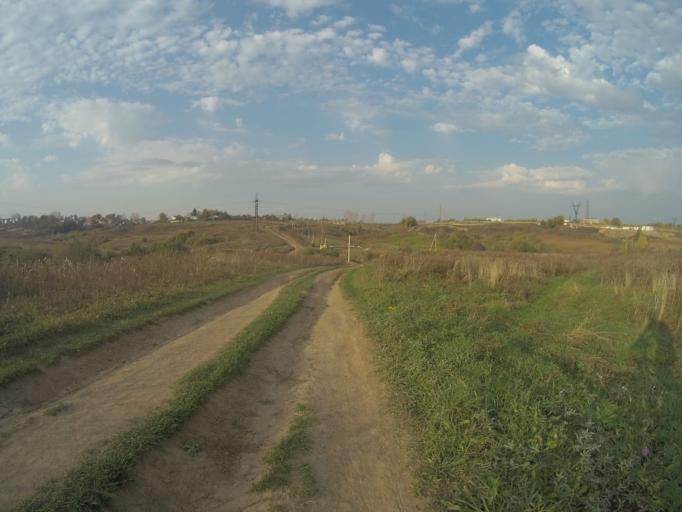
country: RU
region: Vladimir
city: Bogolyubovo
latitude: 56.1836
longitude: 40.5031
